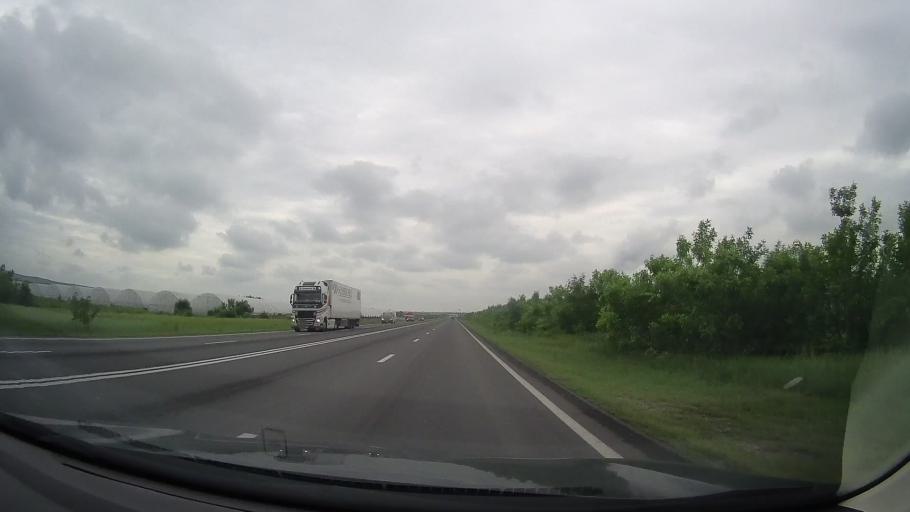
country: RO
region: Dolj
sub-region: Comuna Almaju
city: Almaju
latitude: 44.4248
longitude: 23.6980
